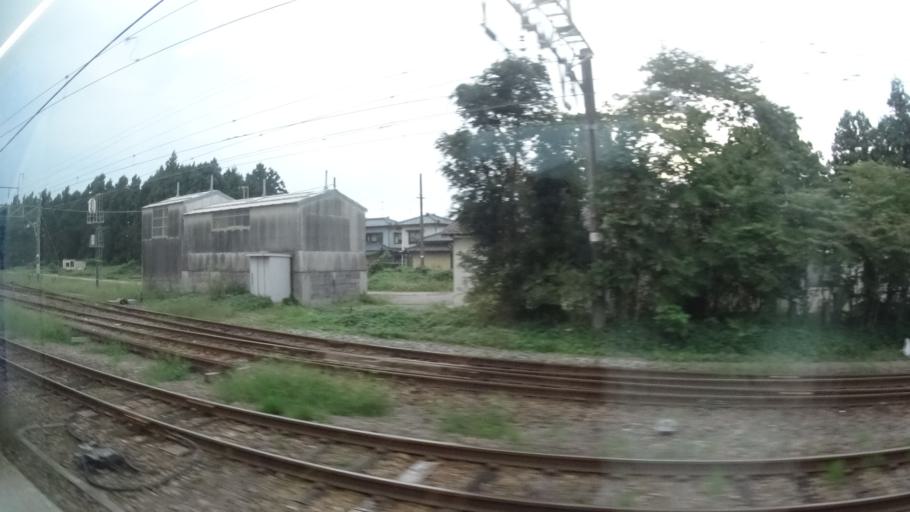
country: JP
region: Niigata
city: Murakami
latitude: 38.2222
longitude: 139.4634
